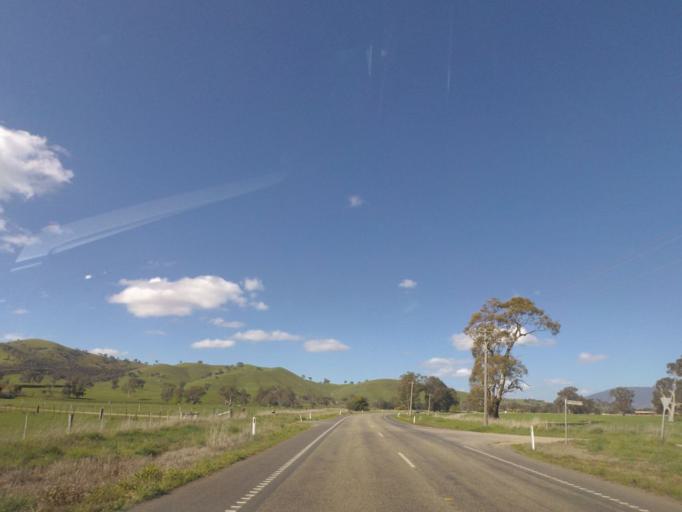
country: AU
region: Victoria
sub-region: Murrindindi
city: Alexandra
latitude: -37.2263
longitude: 145.7467
